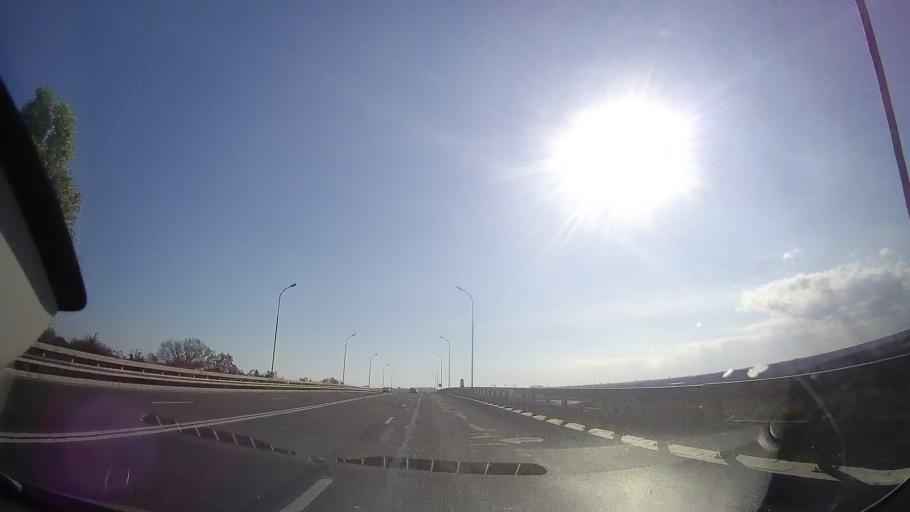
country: RO
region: Constanta
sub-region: Comuna Douazeci si Trei August
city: Dulcesti
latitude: 43.8587
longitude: 28.5757
